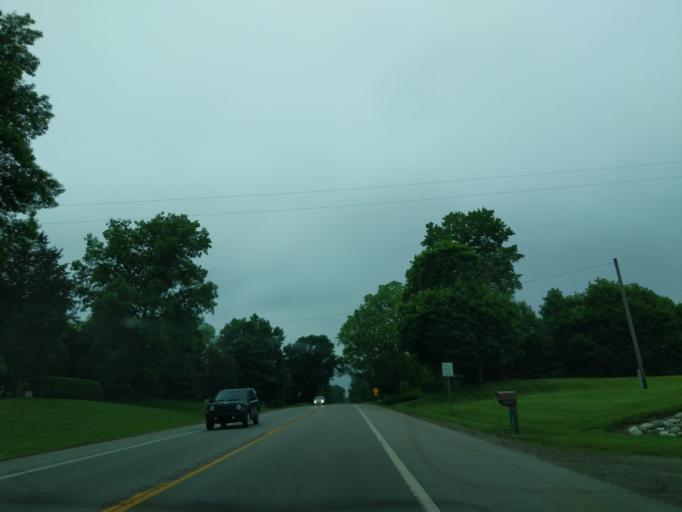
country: US
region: Michigan
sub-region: Branch County
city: Quincy
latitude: 41.9488
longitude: -84.8374
